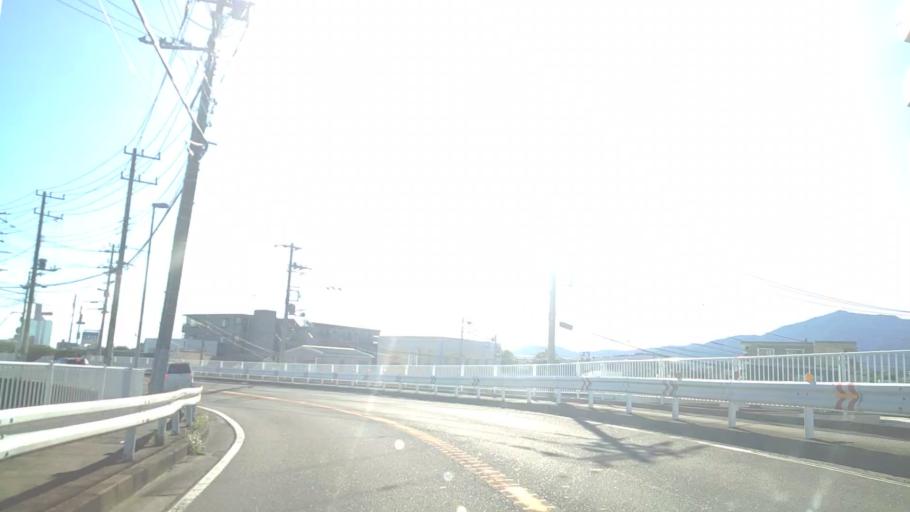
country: JP
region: Kanagawa
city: Atsugi
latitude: 35.4526
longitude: 139.3664
